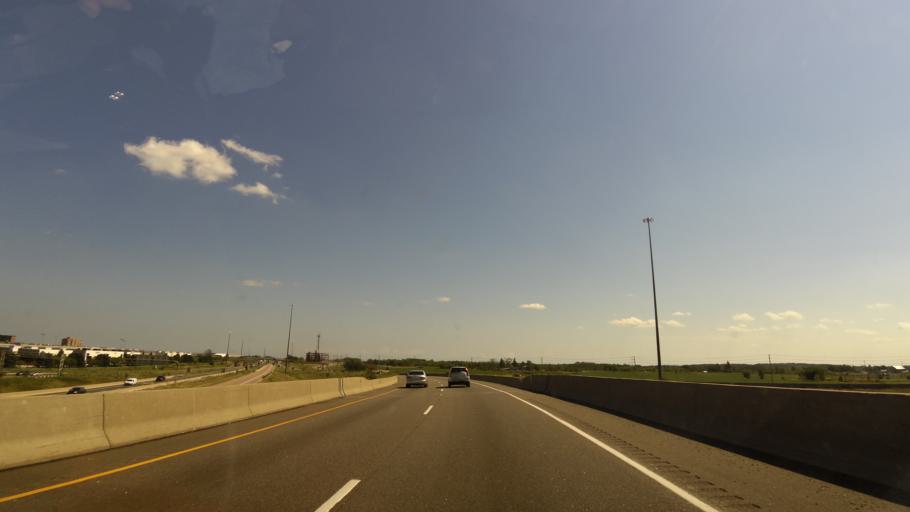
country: CA
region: Ontario
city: Mississauga
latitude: 43.5266
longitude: -79.7236
